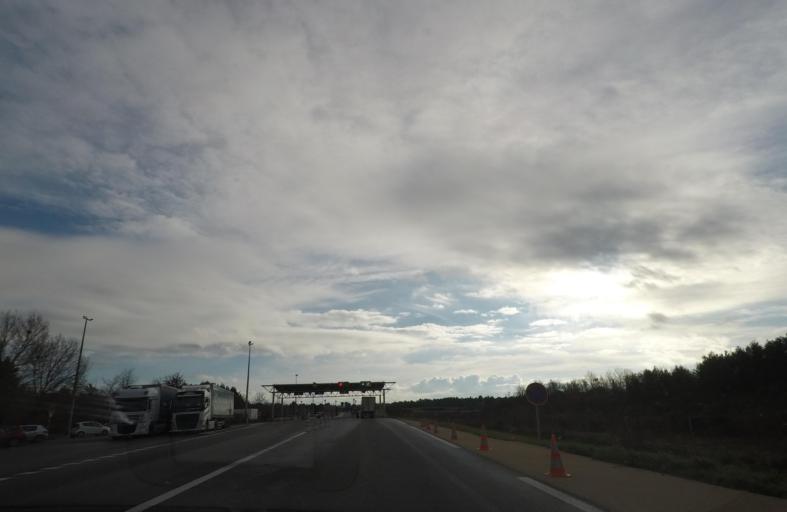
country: FR
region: Centre
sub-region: Departement du Loir-et-Cher
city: Villefranche-sur-Cher
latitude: 47.3252
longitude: 1.7647
